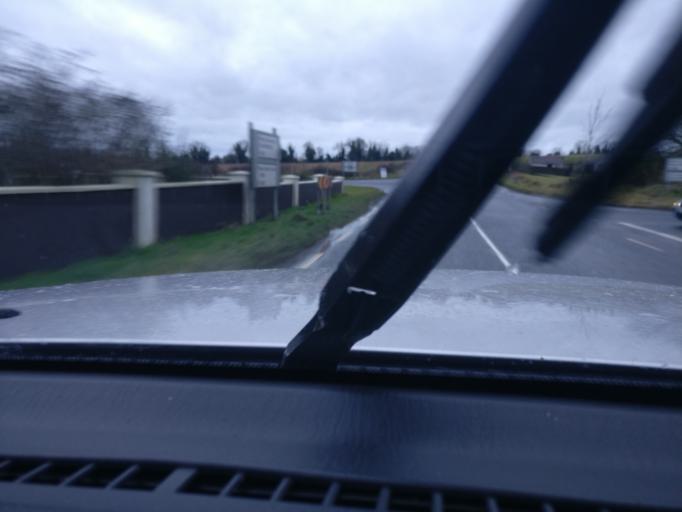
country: IE
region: Leinster
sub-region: An Mhi
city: Trim
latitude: 53.5023
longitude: -6.8545
